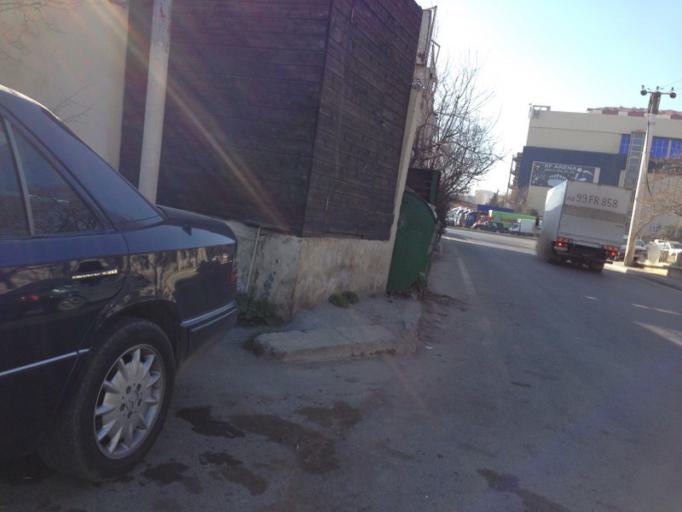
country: AZ
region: Baki
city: Binagadi
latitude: 40.4200
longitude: 49.8566
